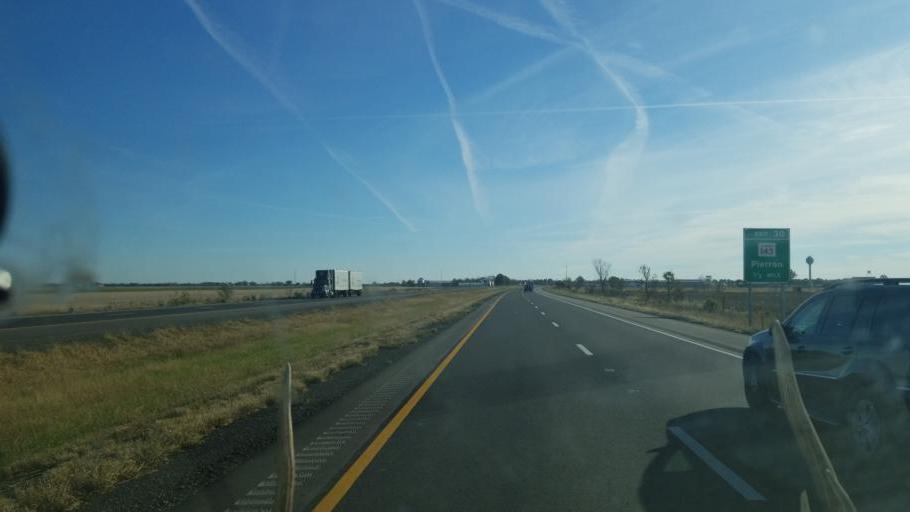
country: US
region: Illinois
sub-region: Madison County
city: Highland
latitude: 38.7864
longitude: -89.6455
